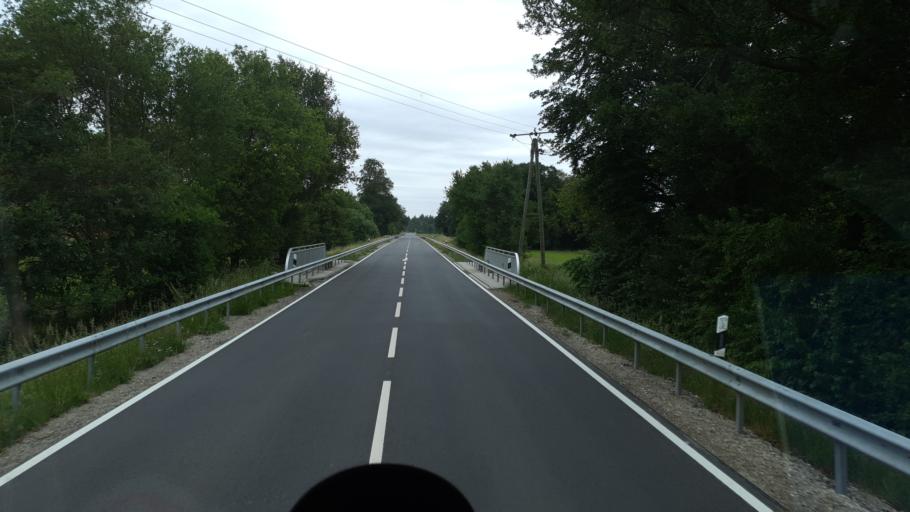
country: NL
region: Overijssel
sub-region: Gemeente Losser
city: Losser
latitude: 52.2704
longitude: 7.0546
